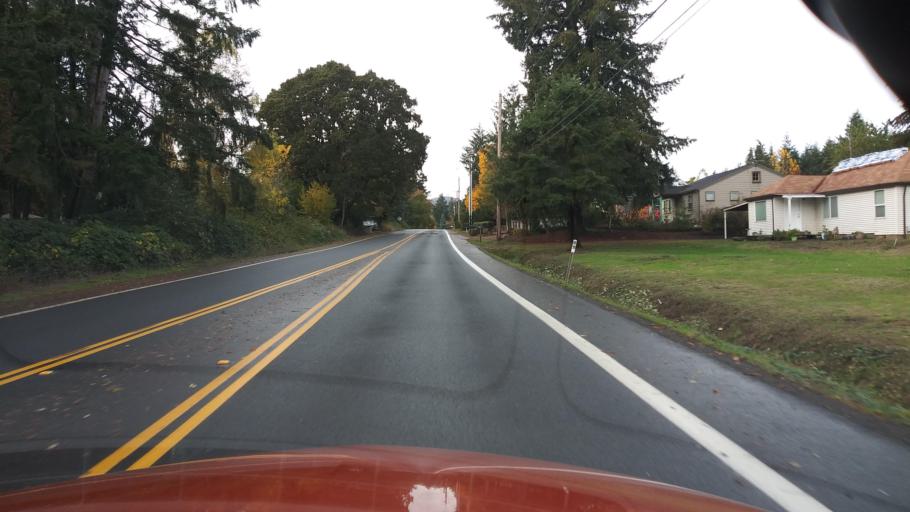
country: US
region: Oregon
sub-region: Washington County
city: Forest Grove
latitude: 45.5300
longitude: -123.1270
